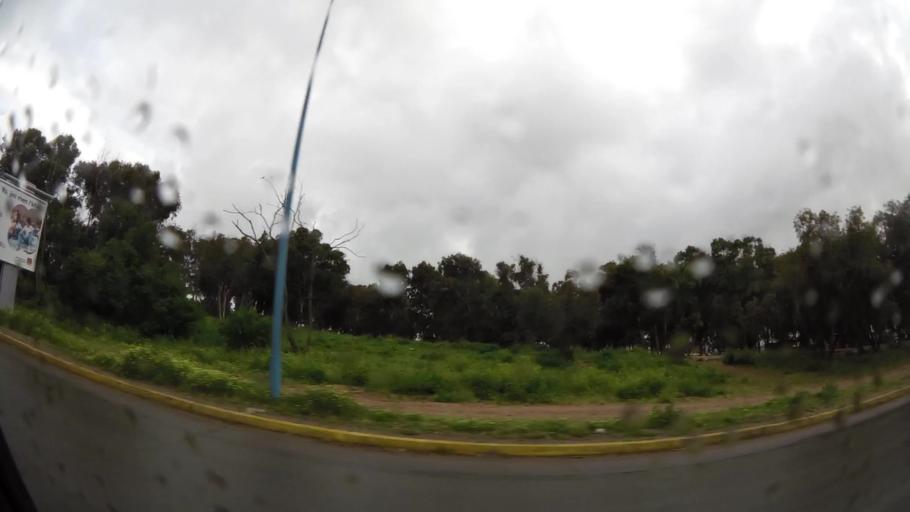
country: MA
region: Grand Casablanca
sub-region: Mohammedia
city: Mohammedia
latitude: 33.6777
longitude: -7.4118
